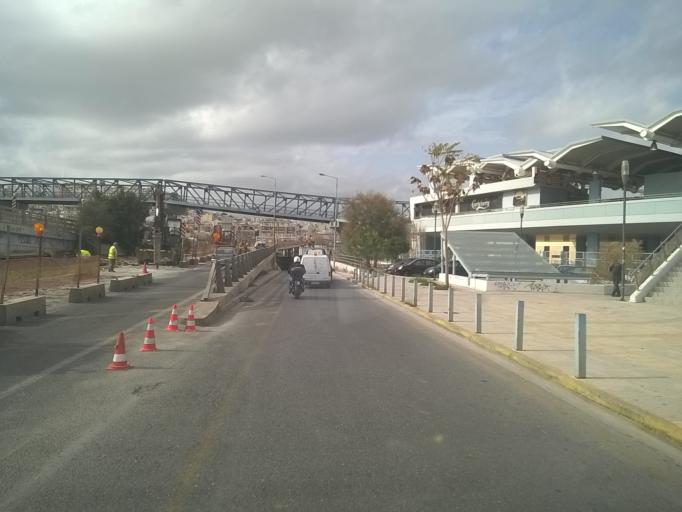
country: GR
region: Attica
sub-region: Nomarchia Athinas
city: Moskhaton
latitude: 37.9446
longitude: 23.6652
